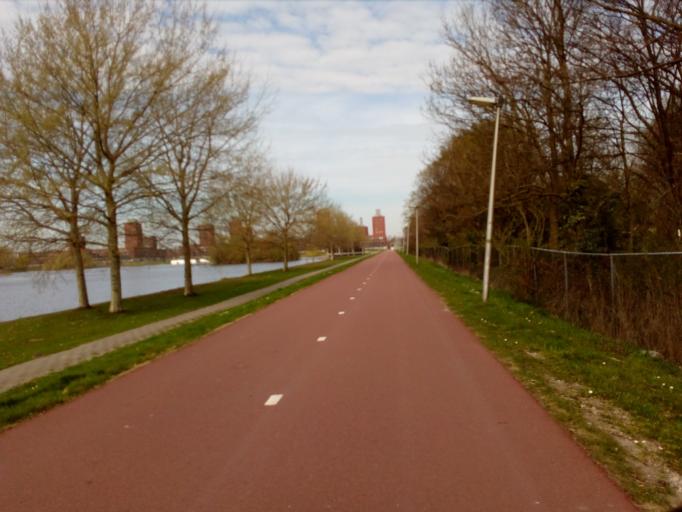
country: NL
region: South Holland
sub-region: Gemeente Den Haag
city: Ypenburg
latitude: 52.0382
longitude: 4.3767
